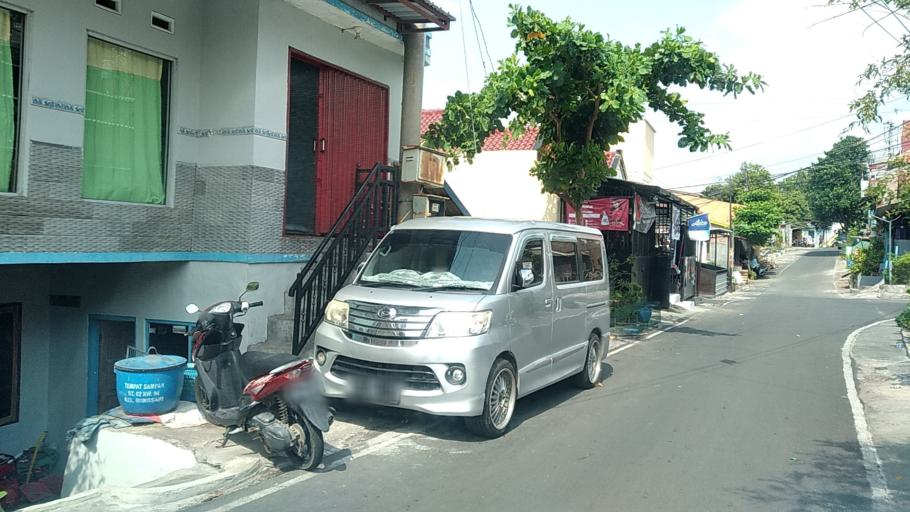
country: ID
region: Central Java
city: Semarang
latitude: -6.9929
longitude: 110.3947
